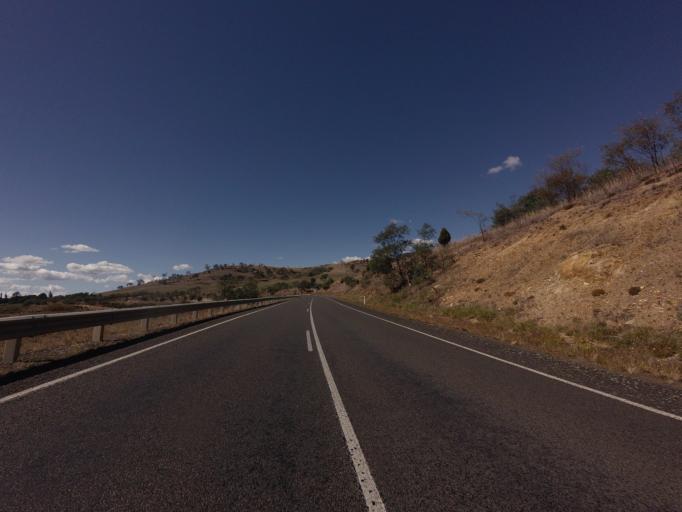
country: AU
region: Tasmania
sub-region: Break O'Day
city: St Helens
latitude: -41.7289
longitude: 147.8225
